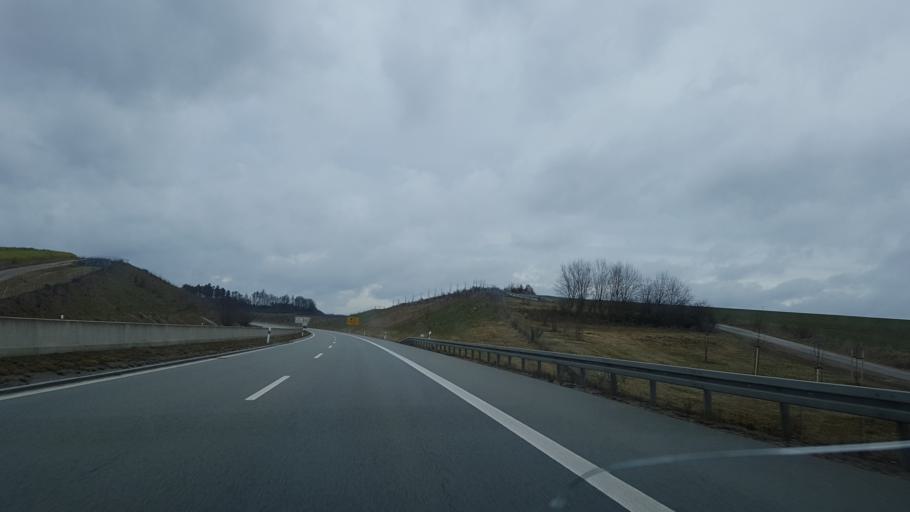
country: DE
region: Bavaria
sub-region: Lower Bavaria
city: Ergoldsbach
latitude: 48.7029
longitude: 12.1781
